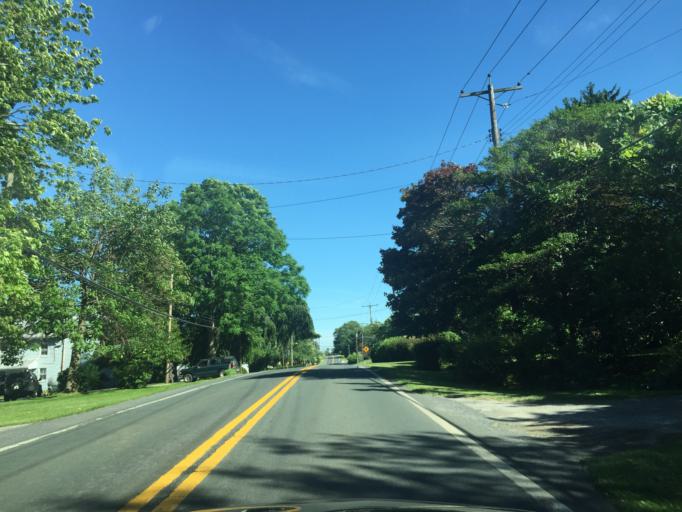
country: US
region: Maryland
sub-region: Carroll County
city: Westminster
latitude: 39.5263
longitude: -76.9259
